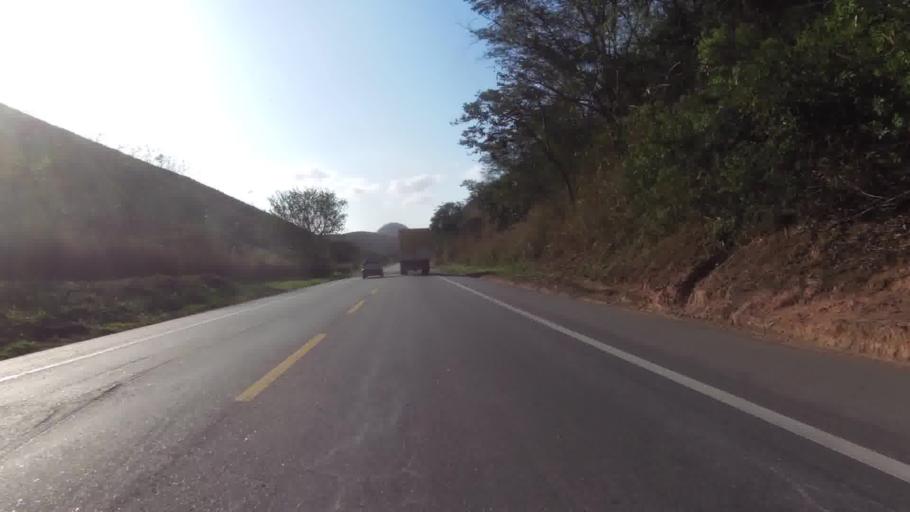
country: BR
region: Espirito Santo
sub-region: Mimoso Do Sul
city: Mimoso do Sul
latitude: -21.1827
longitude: -41.2954
